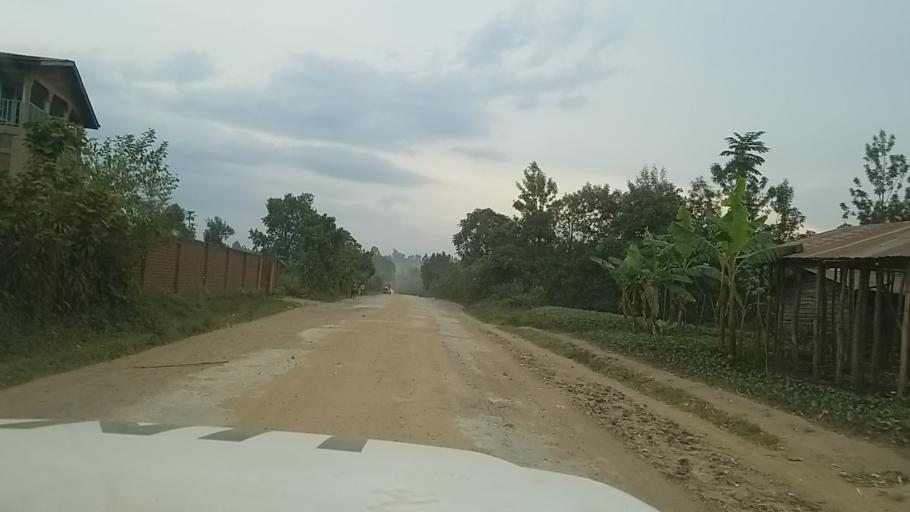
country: CD
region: South Kivu
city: Bukavu
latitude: -2.2592
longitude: 28.8228
